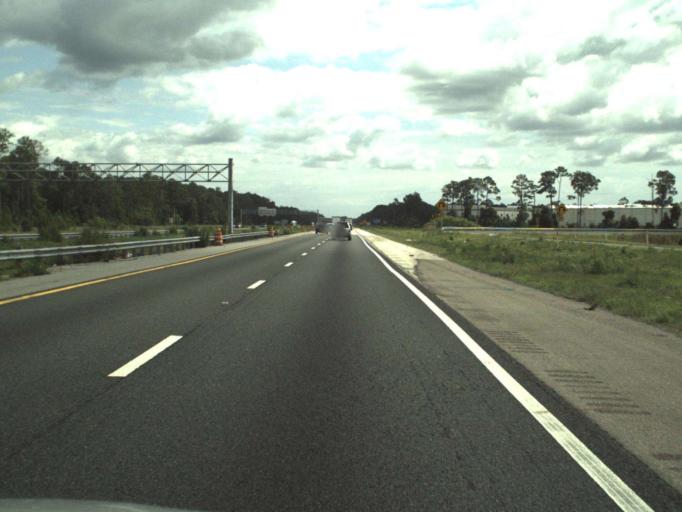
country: US
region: Florida
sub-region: Volusia County
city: Lake Helen
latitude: 29.0181
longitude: -81.2310
